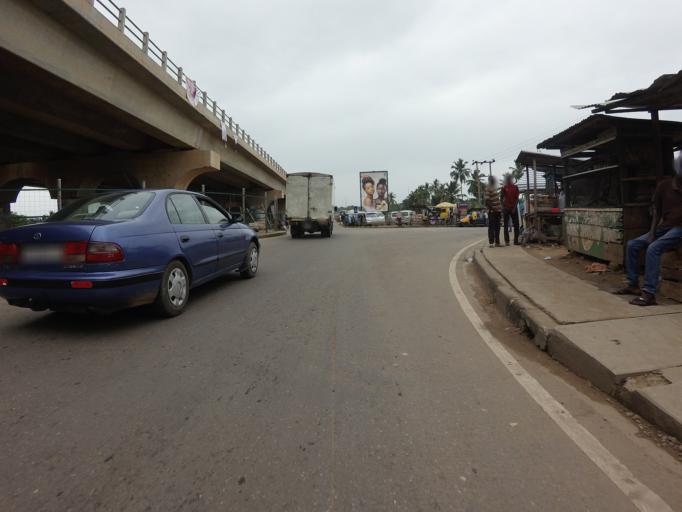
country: GH
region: Eastern
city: Suhum
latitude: 6.0357
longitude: -0.4554
